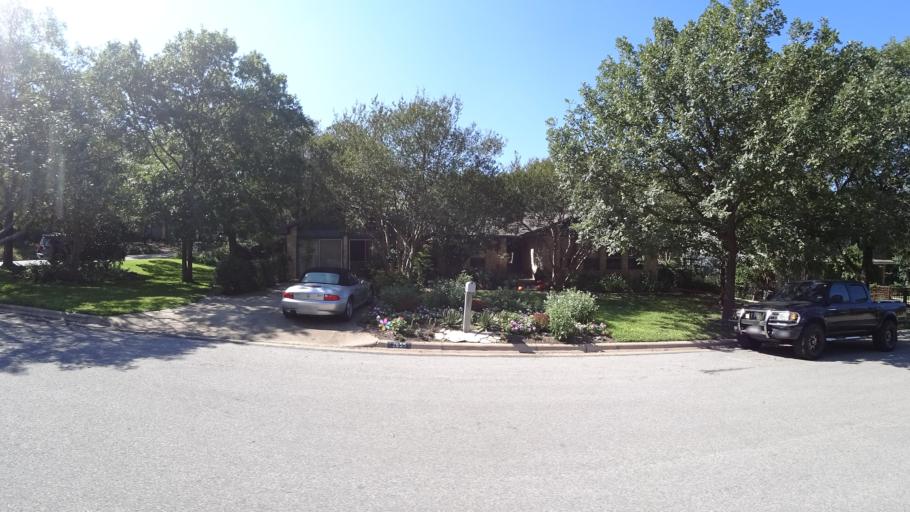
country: US
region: Texas
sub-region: Travis County
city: Rollingwood
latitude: 30.2517
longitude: -97.7925
